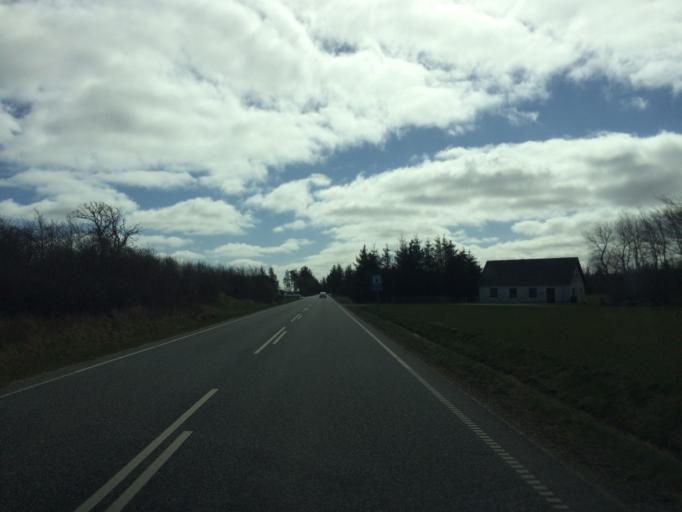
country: DK
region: Central Jutland
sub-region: Holstebro Kommune
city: Ulfborg
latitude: 56.3065
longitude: 8.1830
